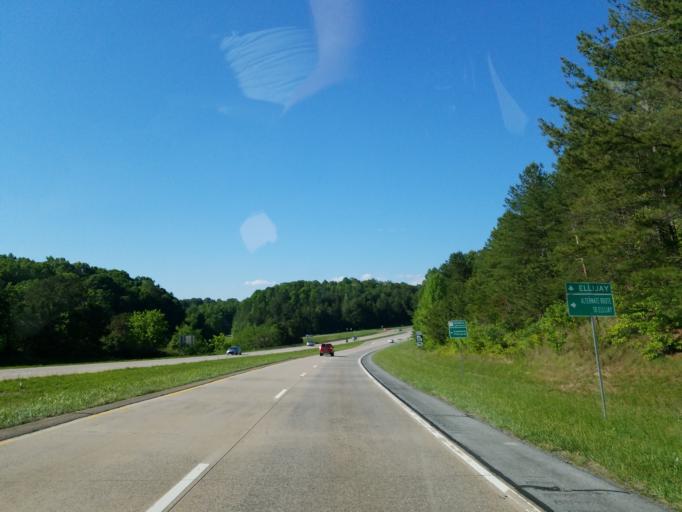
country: US
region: Georgia
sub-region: Gilmer County
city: Ellijay
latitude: 34.6176
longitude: -84.5178
